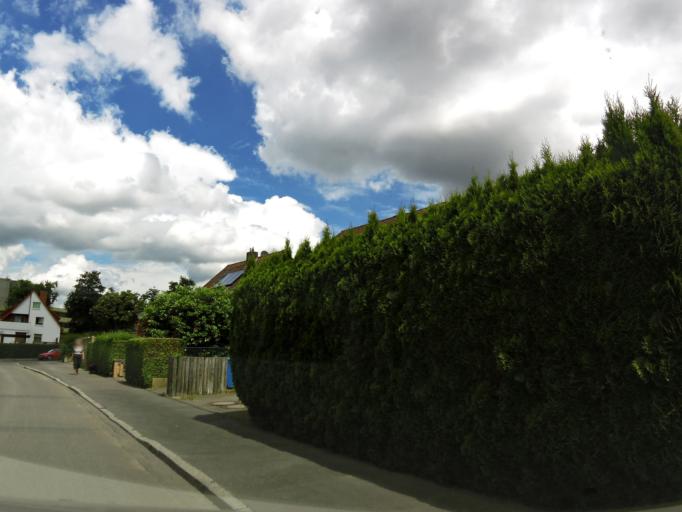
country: DE
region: Lower Saxony
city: Goettingen
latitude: 51.5198
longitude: 9.9477
